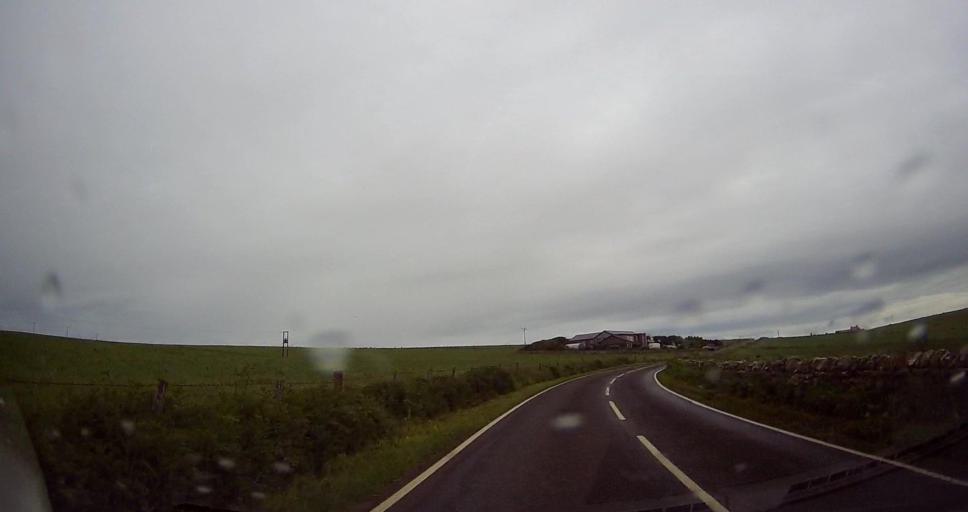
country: GB
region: Scotland
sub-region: Orkney Islands
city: Stromness
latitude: 59.0177
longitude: -3.3049
